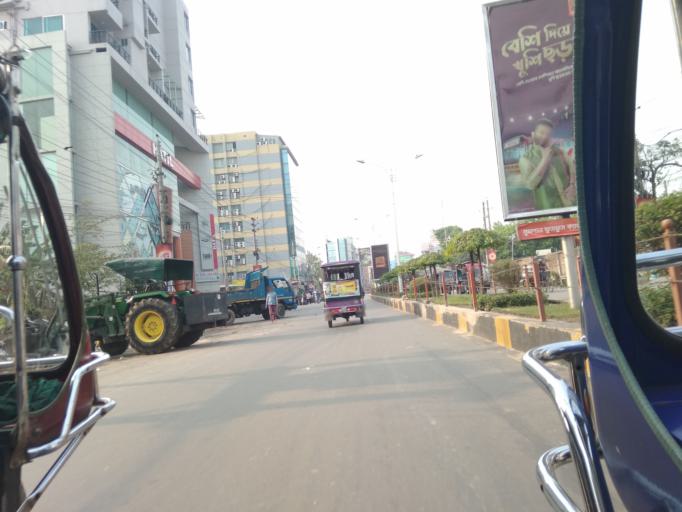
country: BD
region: Khulna
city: Khulna
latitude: 22.8162
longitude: 89.5541
